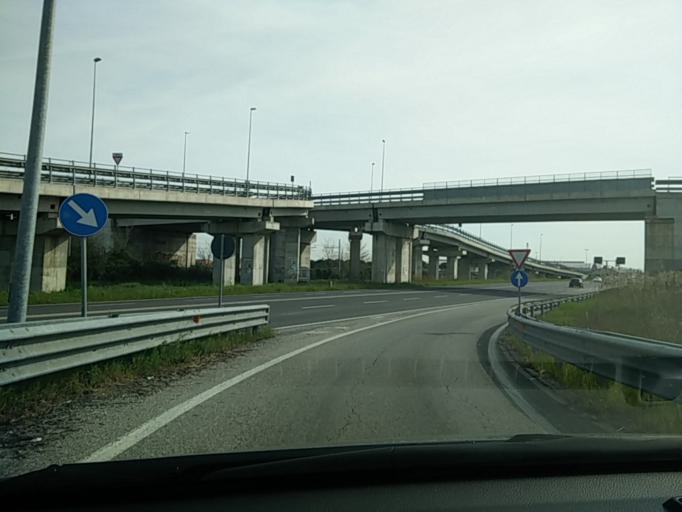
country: IT
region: Emilia-Romagna
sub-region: Provincia di Rimini
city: Santa Giustina
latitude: 44.0700
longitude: 12.5126
